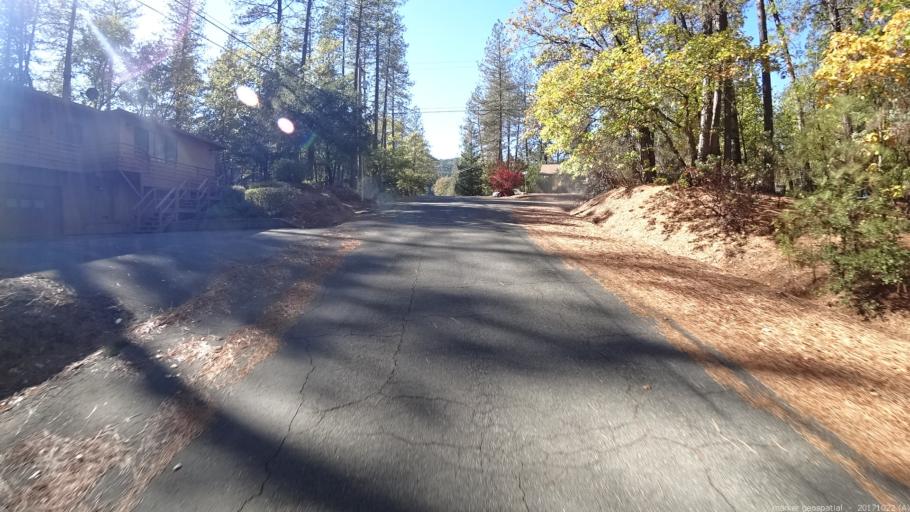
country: US
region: California
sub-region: Shasta County
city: Central Valley (historical)
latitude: 40.8861
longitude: -122.3905
